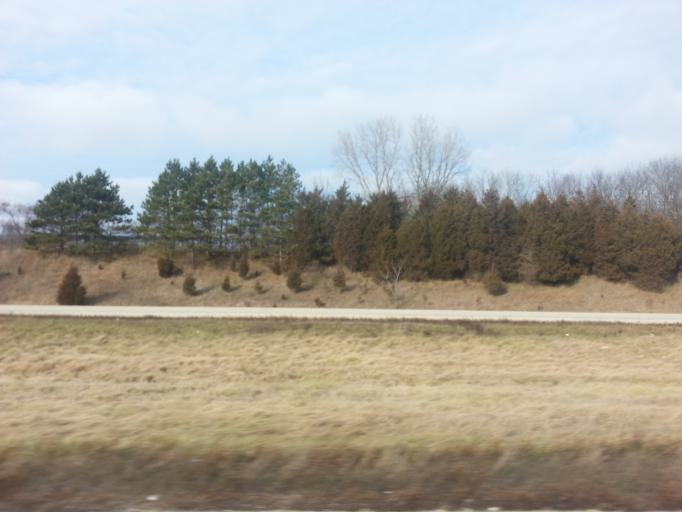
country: US
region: Illinois
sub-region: Winnebago County
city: Cherry Valley
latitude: 42.2031
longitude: -89.0172
